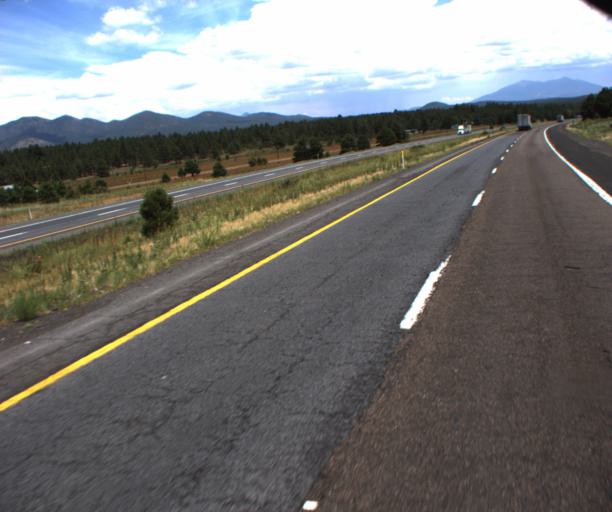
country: US
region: Arizona
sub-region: Coconino County
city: Parks
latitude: 35.2638
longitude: -112.0641
